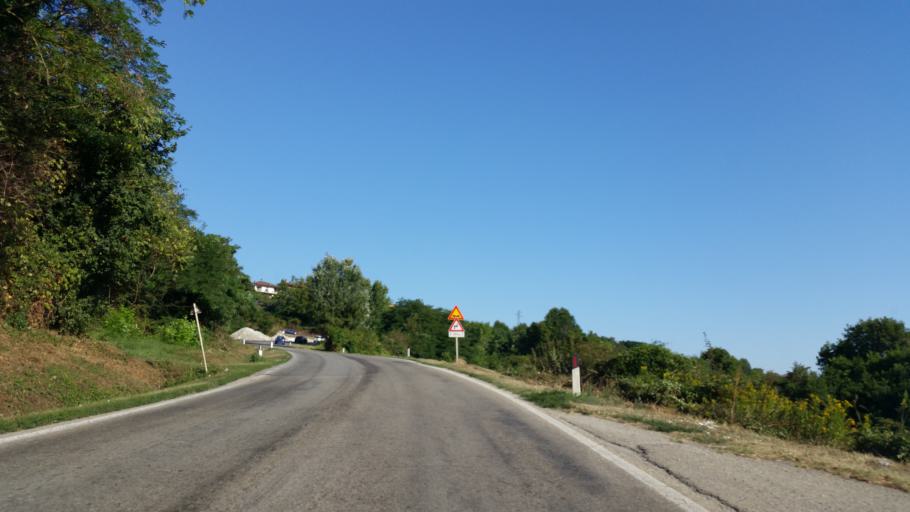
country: IT
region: Piedmont
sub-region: Provincia di Cuneo
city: Roreto
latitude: 44.6702
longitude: 7.8473
